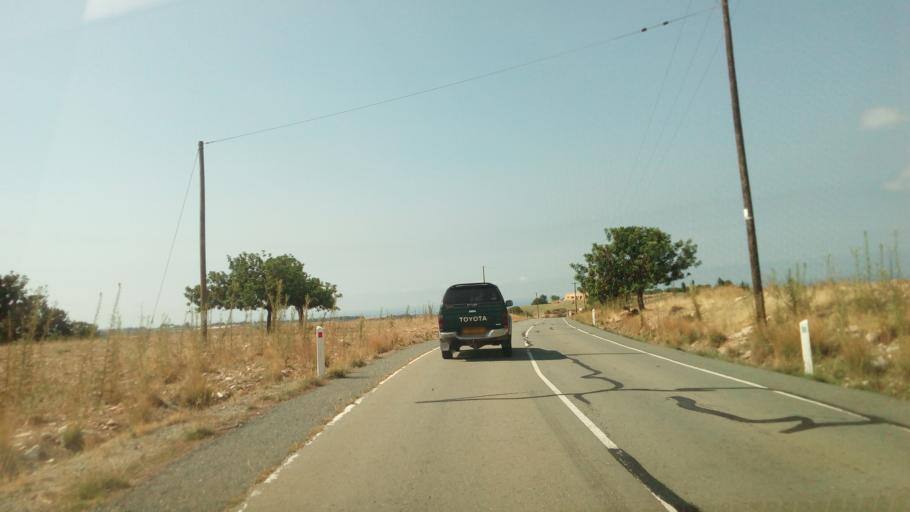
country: CY
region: Limassol
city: Pissouri
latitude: 34.7365
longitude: 32.5756
